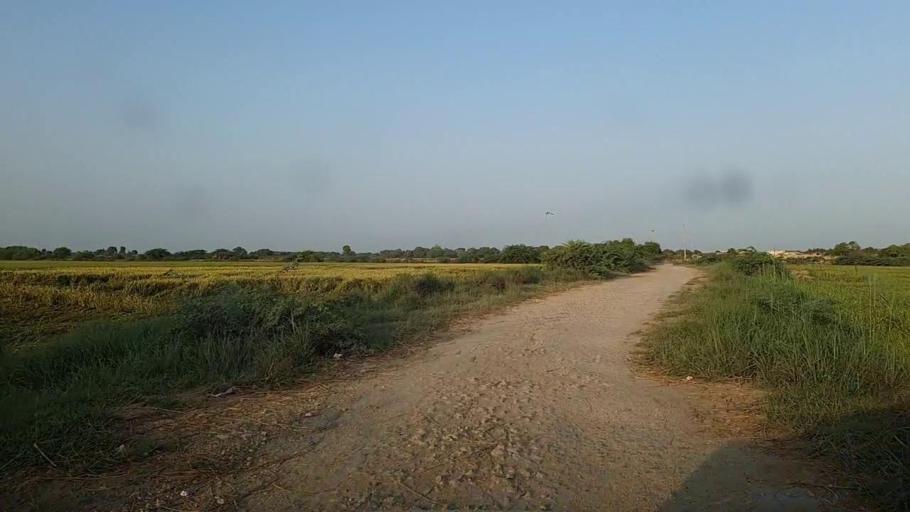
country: PK
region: Sindh
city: Mirpur Batoro
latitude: 24.7355
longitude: 68.4112
